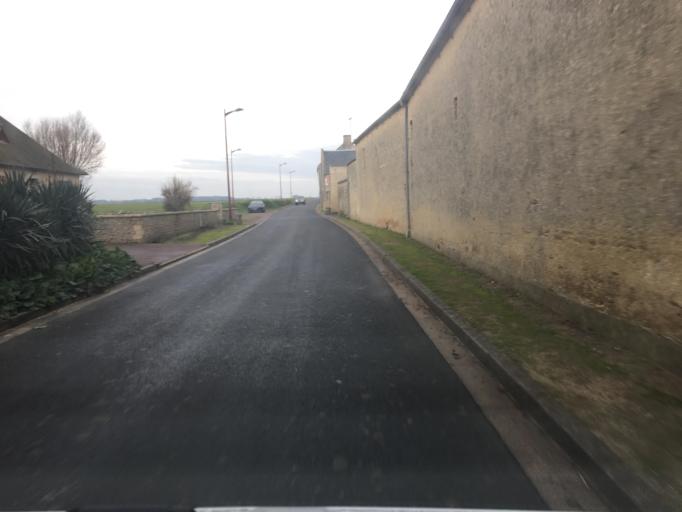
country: FR
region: Lower Normandy
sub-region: Departement du Calvados
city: Ver-sur-Mer
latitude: 49.3273
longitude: -0.5706
